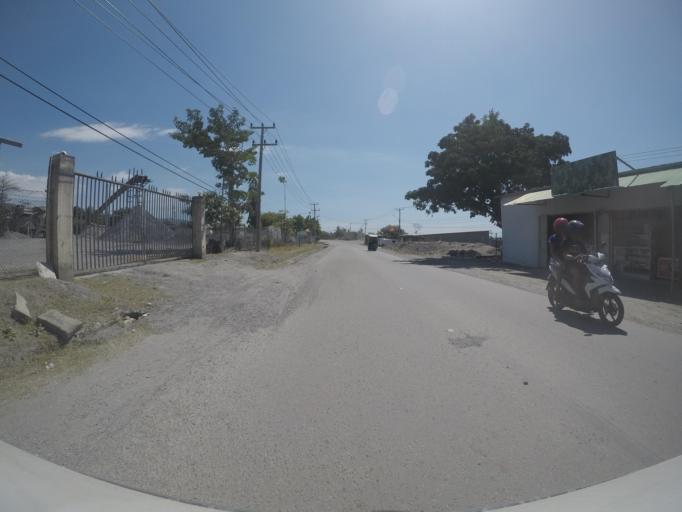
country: TL
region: Liquica
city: Liquica
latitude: -8.5901
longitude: 125.3376
